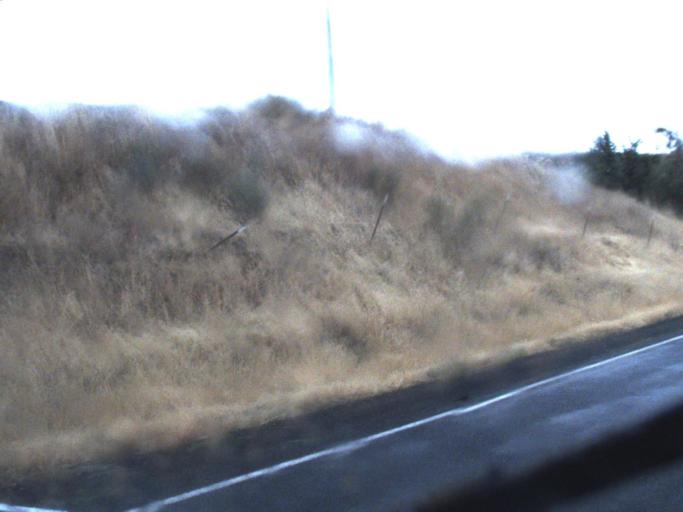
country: US
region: Washington
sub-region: Whitman County
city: Colfax
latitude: 47.0659
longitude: -117.5276
